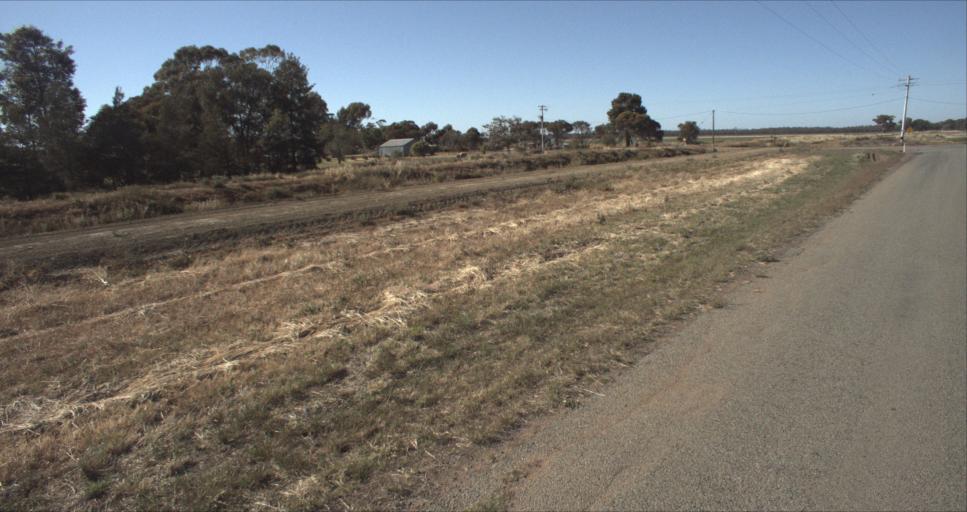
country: AU
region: New South Wales
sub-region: Leeton
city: Leeton
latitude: -34.5825
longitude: 146.3085
